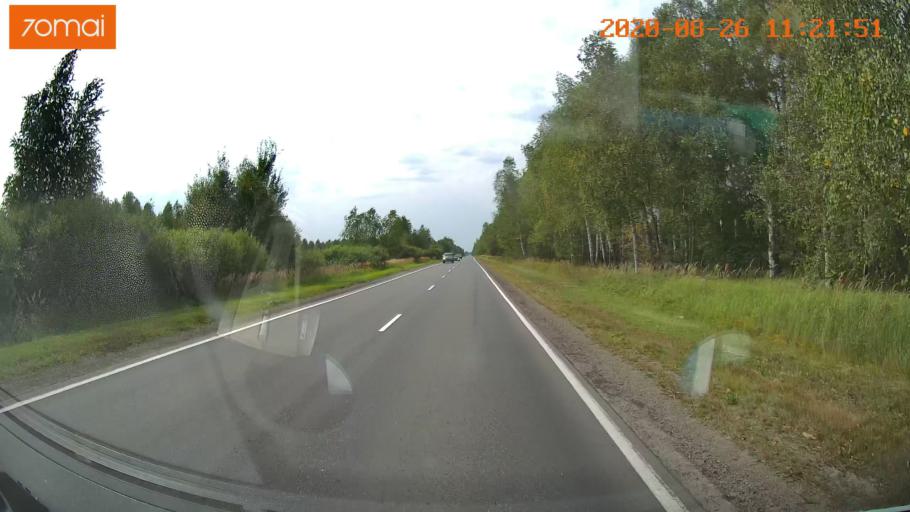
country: RU
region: Rjazan
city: Shilovo
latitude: 54.3712
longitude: 41.0375
